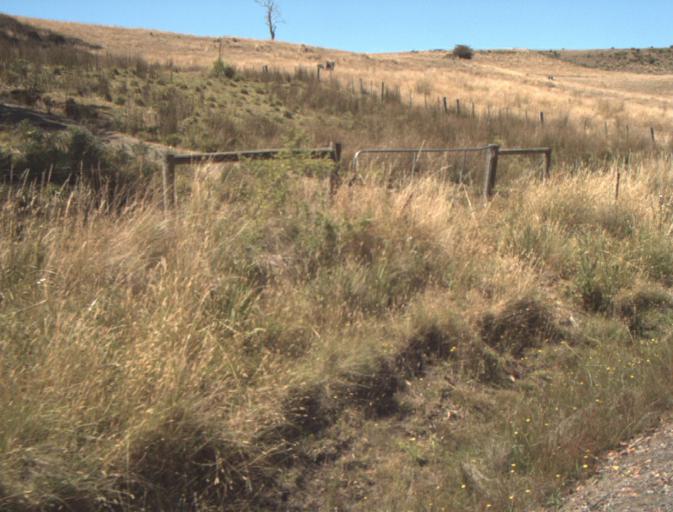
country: AU
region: Tasmania
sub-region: Launceston
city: Newstead
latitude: -41.3569
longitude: 147.3029
